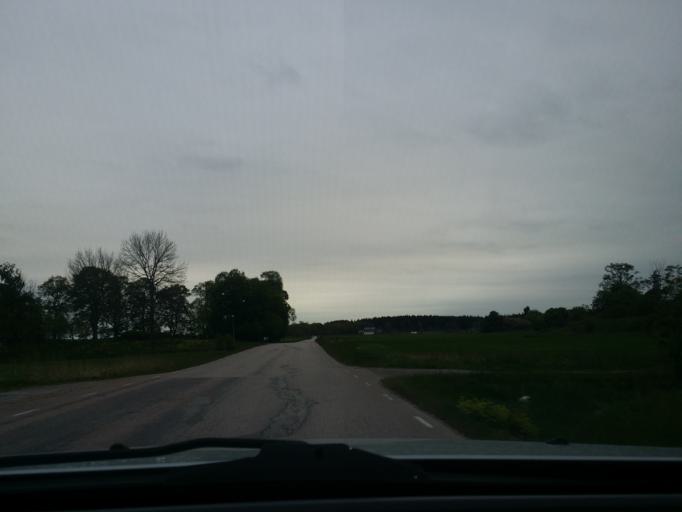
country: SE
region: Vaestmanland
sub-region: Hallstahammars Kommun
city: Kolback
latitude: 59.5370
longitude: 16.3009
